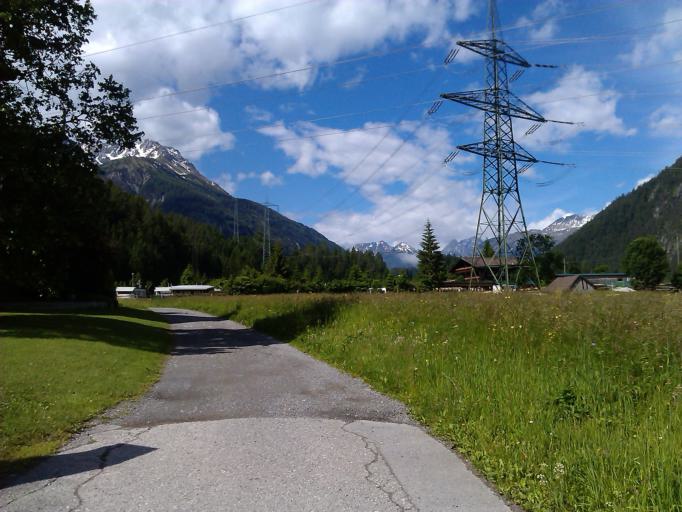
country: AT
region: Tyrol
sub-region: Politischer Bezirk Reutte
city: Biberwier
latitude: 47.3831
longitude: 10.9039
